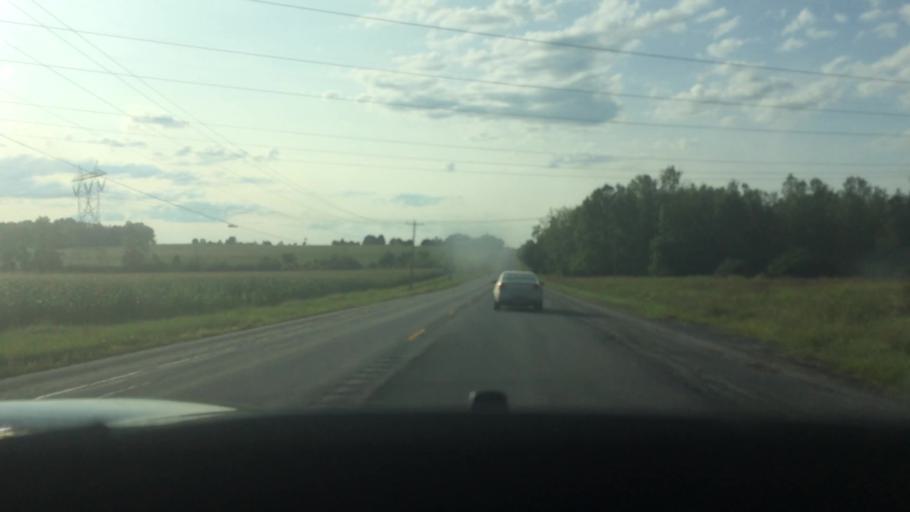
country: US
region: New York
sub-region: St. Lawrence County
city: Canton
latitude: 44.5967
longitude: -75.1895
